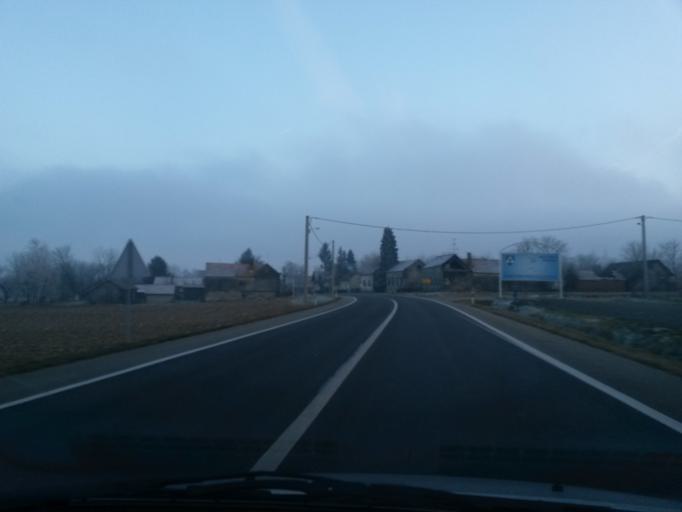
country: HR
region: Varazdinska
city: Ludbreg
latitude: 46.2125
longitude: 16.6931
